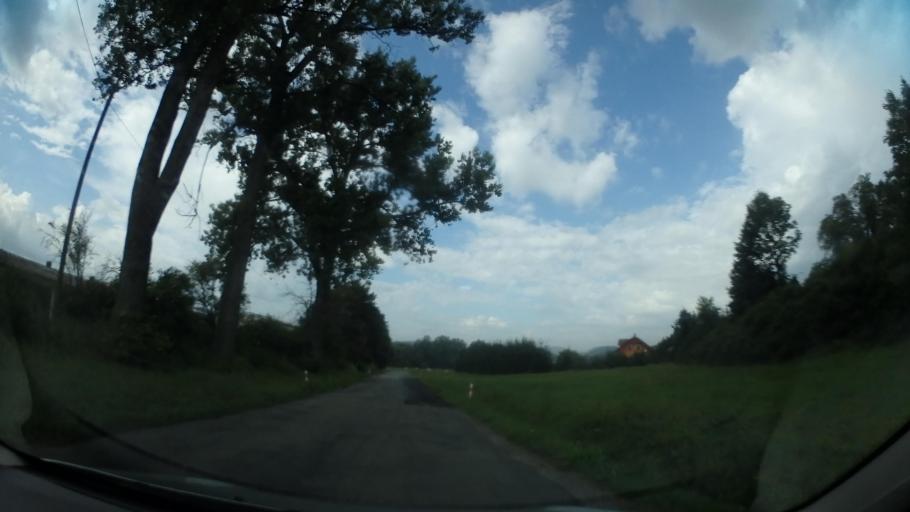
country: CZ
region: Plzensky
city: Horazd'ovice
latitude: 49.2620
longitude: 13.6684
